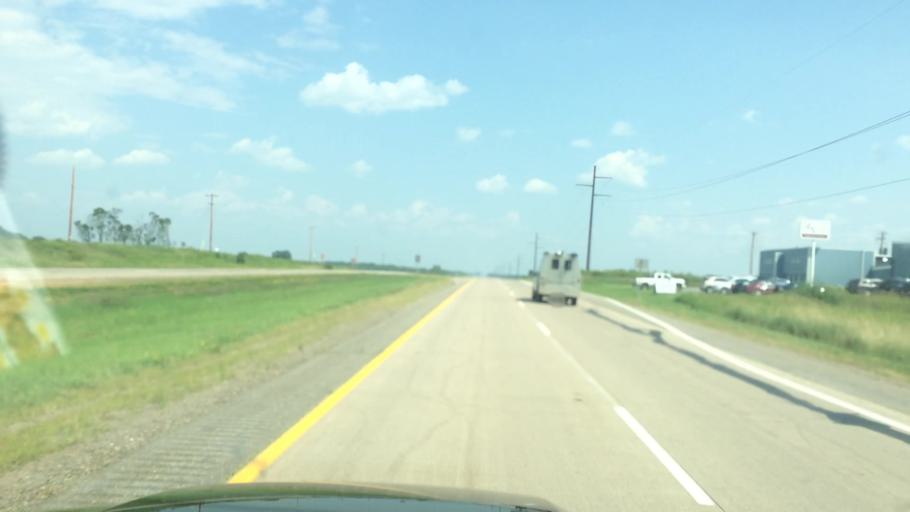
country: US
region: Wisconsin
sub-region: Marathon County
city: Edgar
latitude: 44.9441
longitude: -90.0067
